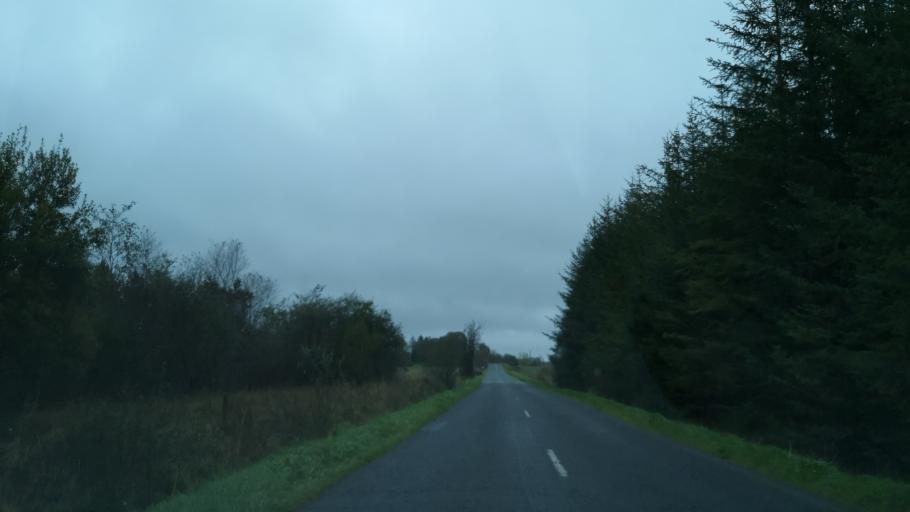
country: IE
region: Connaught
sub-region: Maigh Eo
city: Ballyhaunis
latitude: 53.7963
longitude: -8.7035
